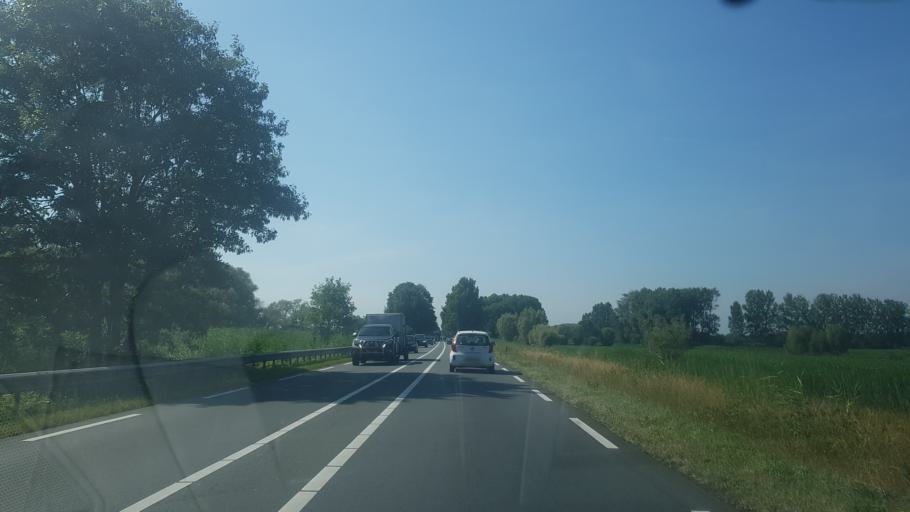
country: NL
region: North Brabant
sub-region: Gemeente Veghel
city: Keldonk
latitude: 51.5892
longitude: 5.5685
